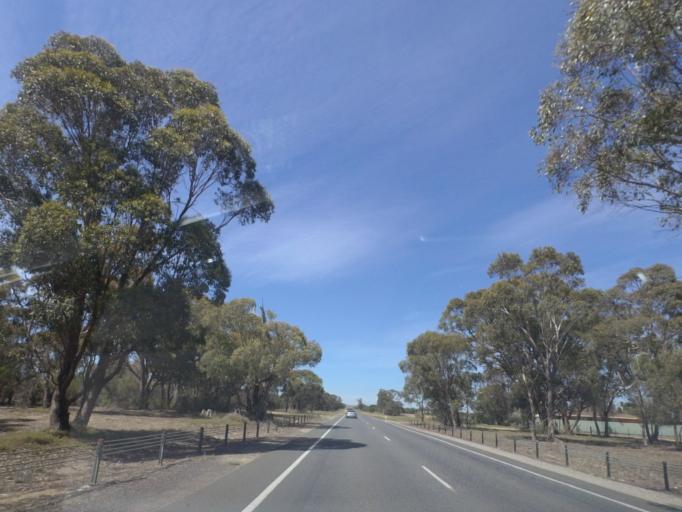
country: AU
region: Victoria
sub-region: Wyndham
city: Little River
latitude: -37.8643
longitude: 144.3854
